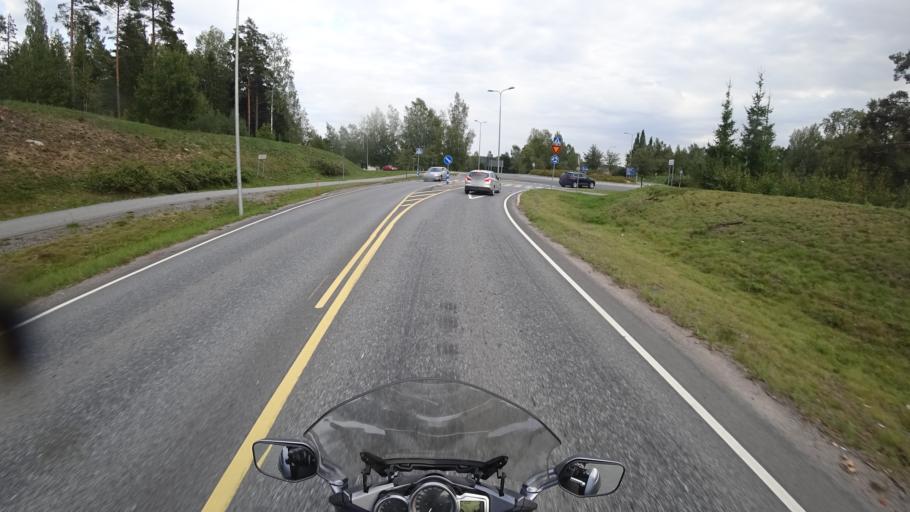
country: FI
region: Uusimaa
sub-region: Raaseporin
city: Karis
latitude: 60.0586
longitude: 23.6428
